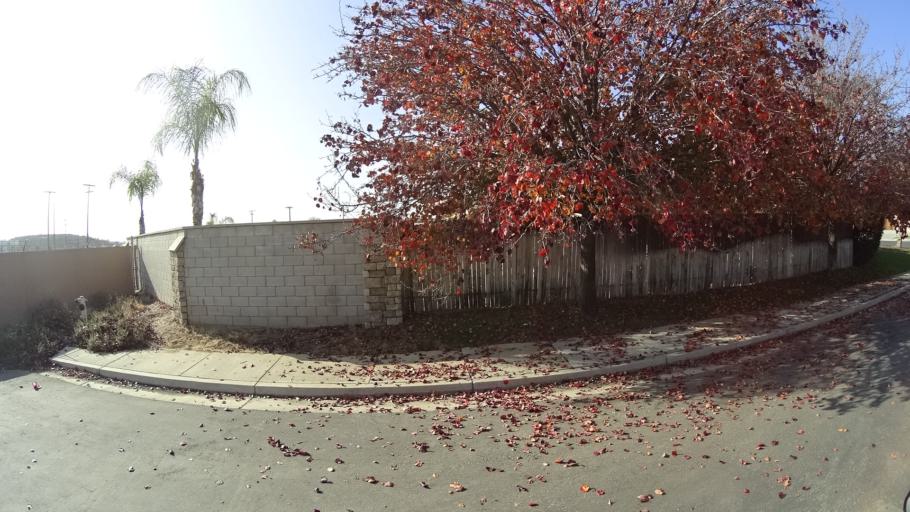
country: US
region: California
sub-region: Kern County
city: Greenacres
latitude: 35.3906
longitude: -119.0688
